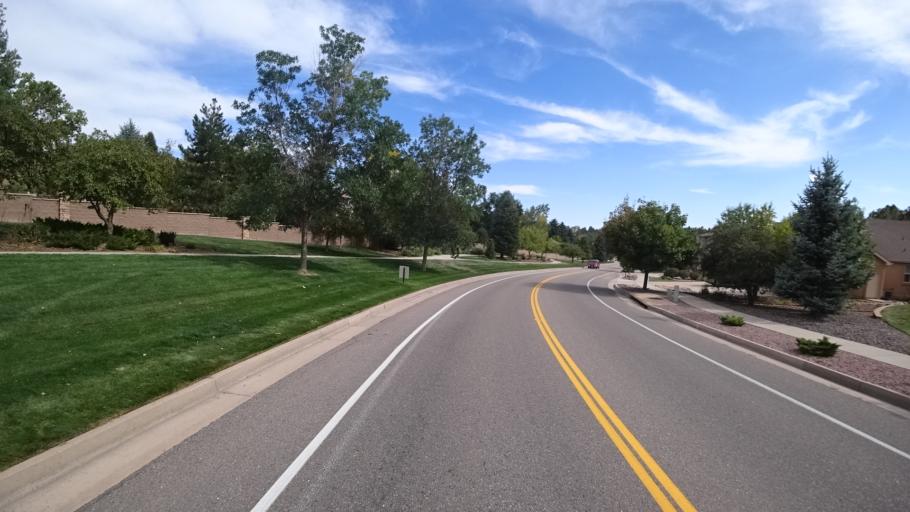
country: US
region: Colorado
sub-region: El Paso County
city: Colorado Springs
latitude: 38.9017
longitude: -104.7843
